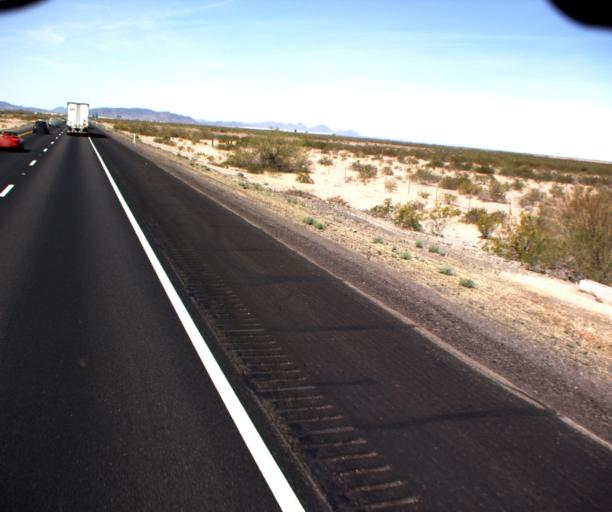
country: US
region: Arizona
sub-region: La Paz County
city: Salome
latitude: 33.6272
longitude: -113.7396
